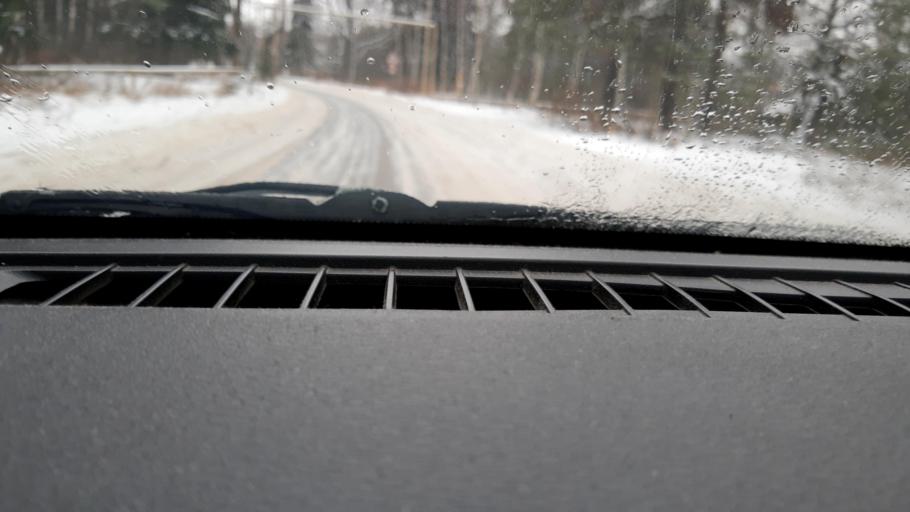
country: RU
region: Nizjnij Novgorod
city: Afonino
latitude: 56.1864
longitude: 44.0796
